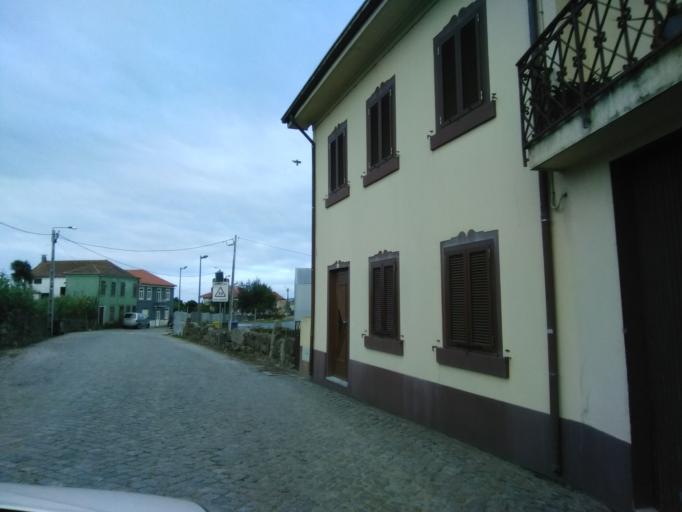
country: PT
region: Porto
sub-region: Matosinhos
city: Lavra
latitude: 41.2677
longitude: -8.7119
